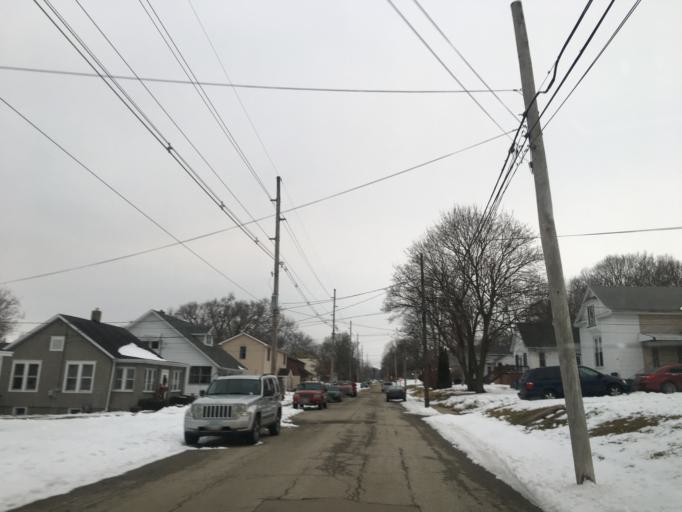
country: US
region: Illinois
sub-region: LaSalle County
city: Peru
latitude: 41.3249
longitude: -89.1307
